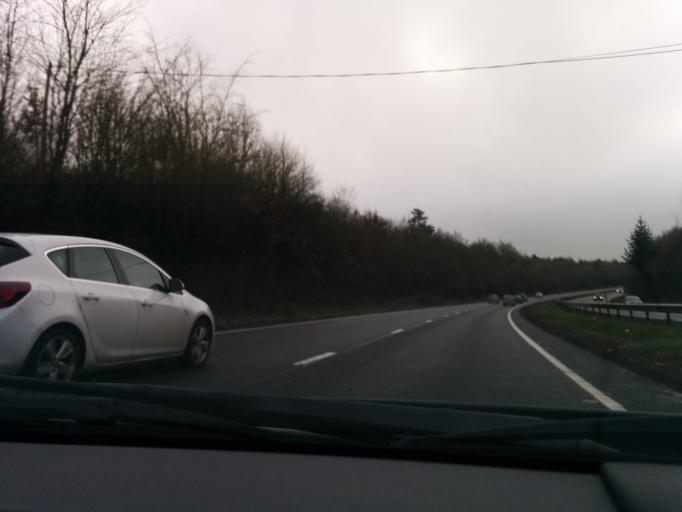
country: GB
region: England
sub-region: Hampshire
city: Highclere
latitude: 51.3403
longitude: -1.3405
